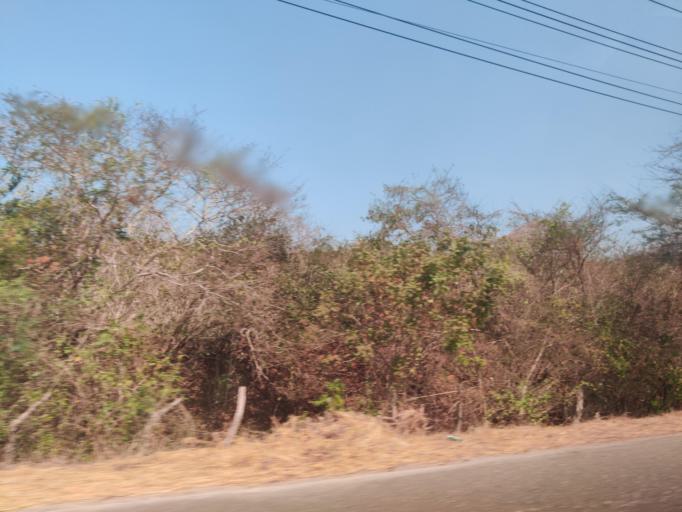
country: CO
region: Bolivar
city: Turbana
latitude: 10.2747
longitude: -75.5478
